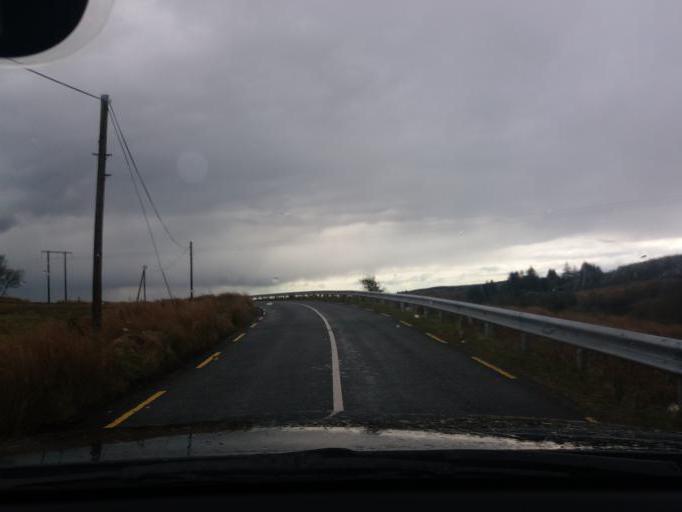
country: IE
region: Ulster
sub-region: An Cabhan
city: Ballyconnell
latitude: 54.1615
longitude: -7.7814
